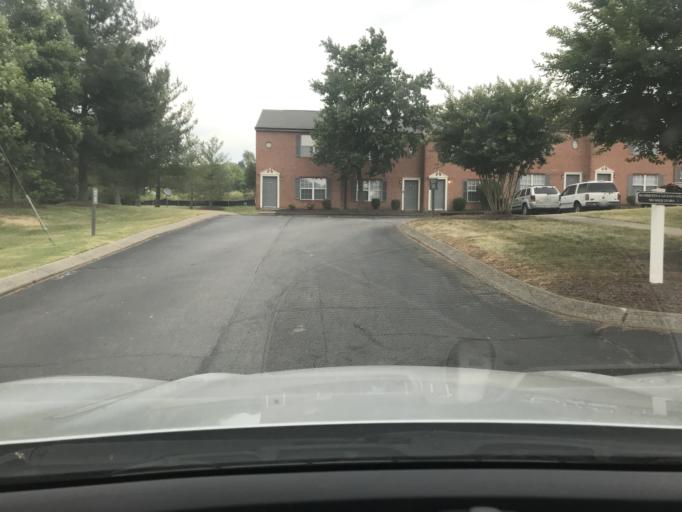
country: US
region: Tennessee
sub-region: Davidson County
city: Goodlettsville
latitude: 36.2971
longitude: -86.7189
